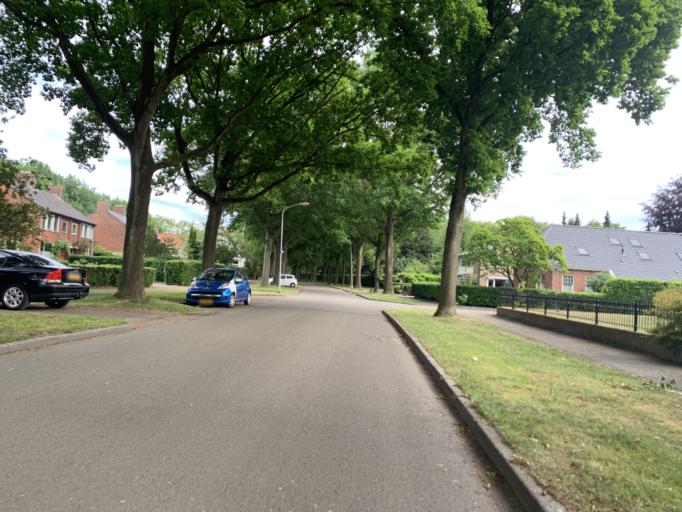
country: NL
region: Groningen
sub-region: Gemeente Haren
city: Haren
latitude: 53.1648
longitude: 6.6154
